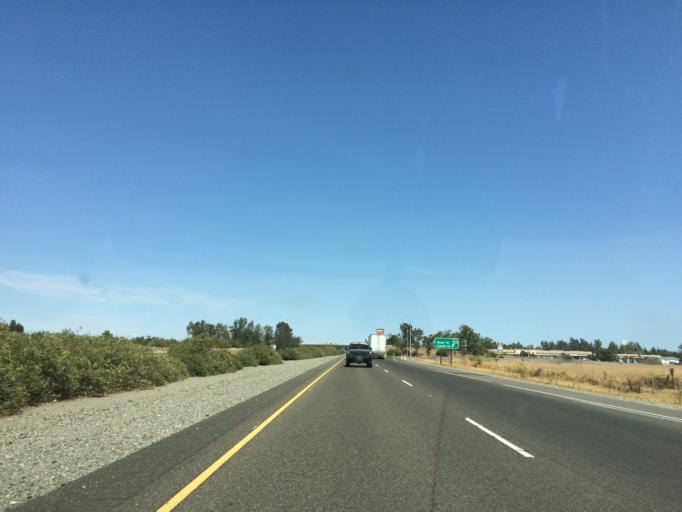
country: US
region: California
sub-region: Glenn County
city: Orland
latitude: 39.7359
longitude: -122.2057
